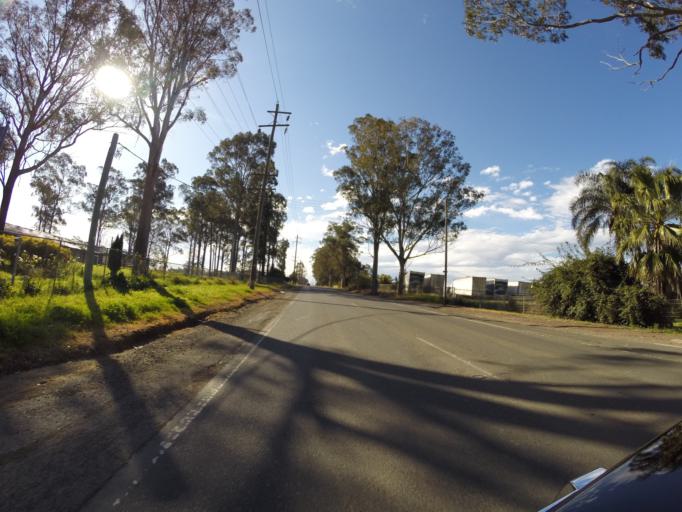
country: AU
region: New South Wales
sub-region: Liverpool
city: Bringelly
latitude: -33.9088
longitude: 150.7874
